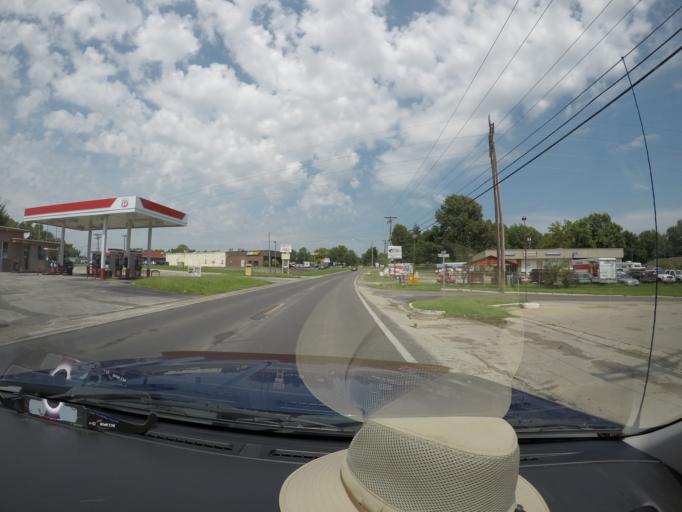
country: US
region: Missouri
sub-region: Lafayette County
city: Lexington
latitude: 39.1671
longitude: -93.8790
